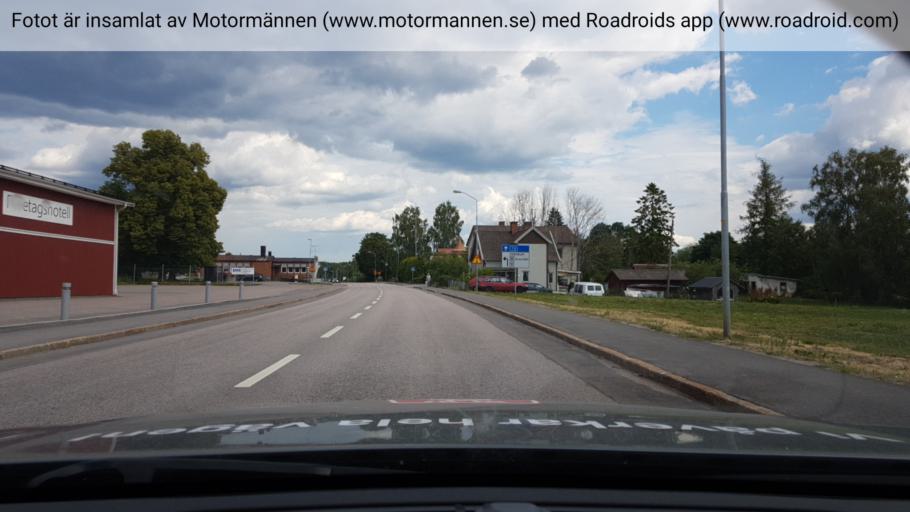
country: SE
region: Uppsala
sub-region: Heby Kommun
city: Morgongava
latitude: 59.9331
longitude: 16.9575
